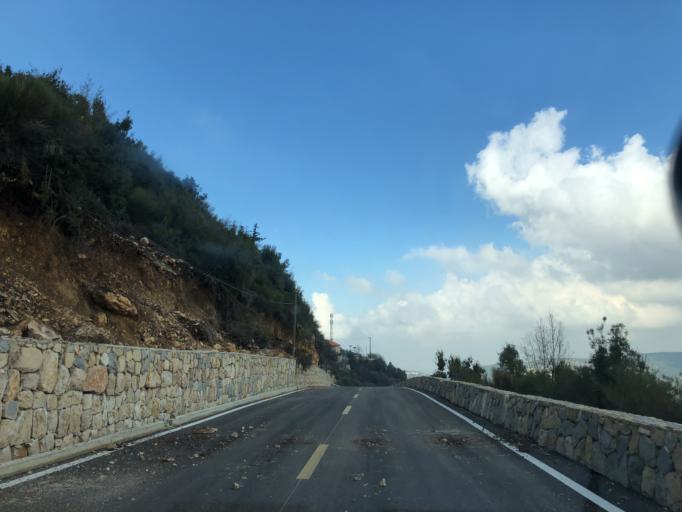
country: LB
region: Liban-Nord
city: Amioun
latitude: 34.2142
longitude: 35.8302
